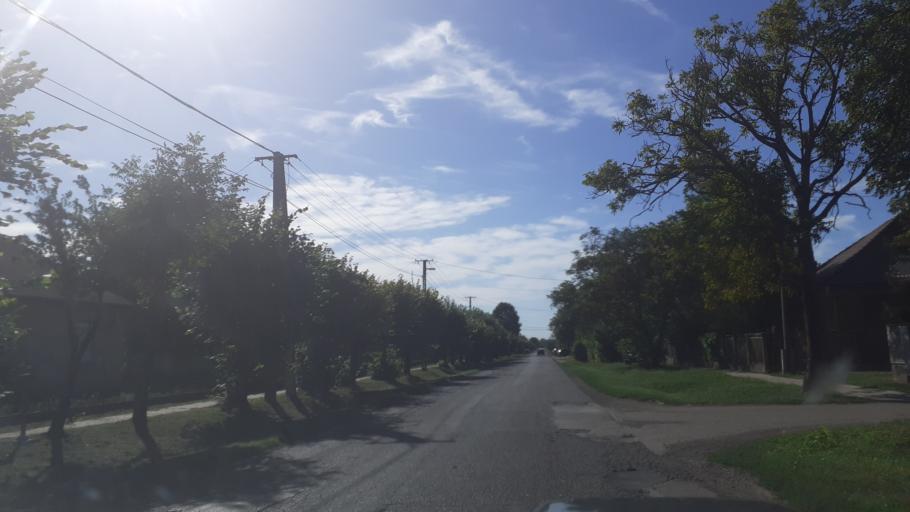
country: HU
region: Fejer
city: Ivancsa
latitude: 47.1901
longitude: 18.7952
